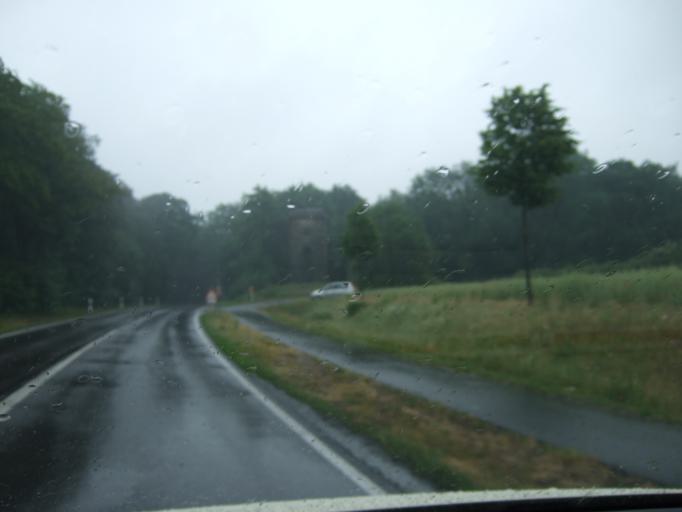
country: DE
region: Saxony-Anhalt
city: Harbke
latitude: 52.2162
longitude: 11.0437
